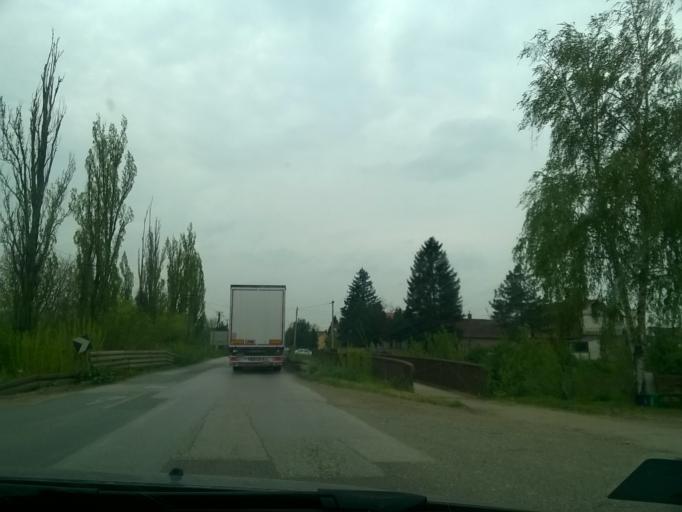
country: RS
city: Jarak
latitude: 44.9121
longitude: 19.7649
